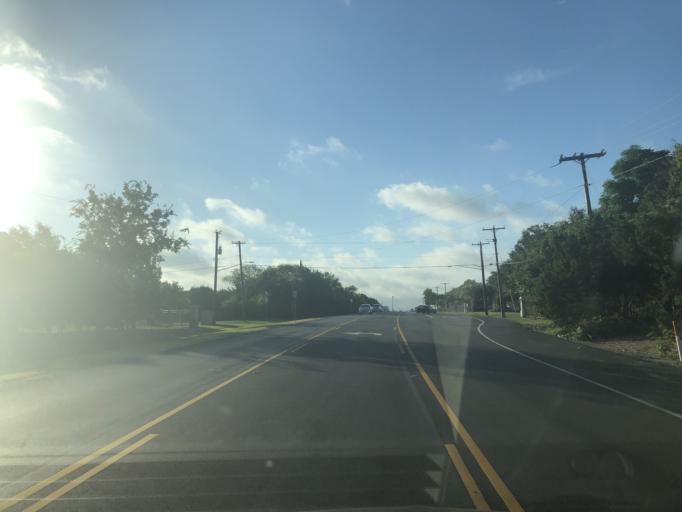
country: US
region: Texas
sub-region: Dallas County
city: Duncanville
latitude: 32.6647
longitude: -96.9478
